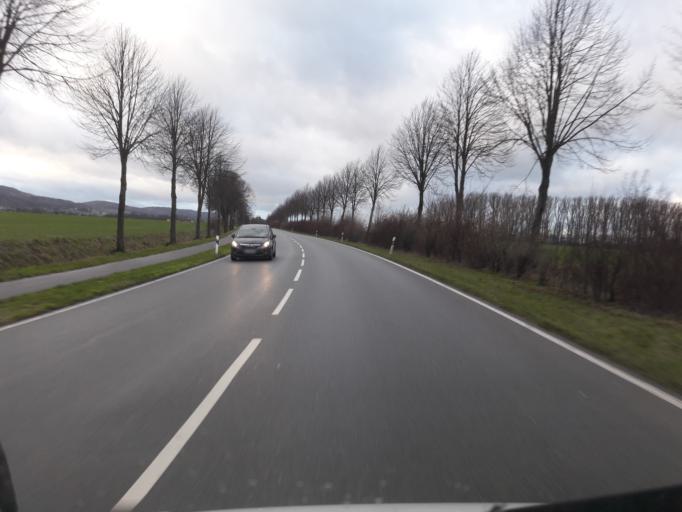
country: DE
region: North Rhine-Westphalia
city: Bad Oeynhausen
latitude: 52.2780
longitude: 8.8278
